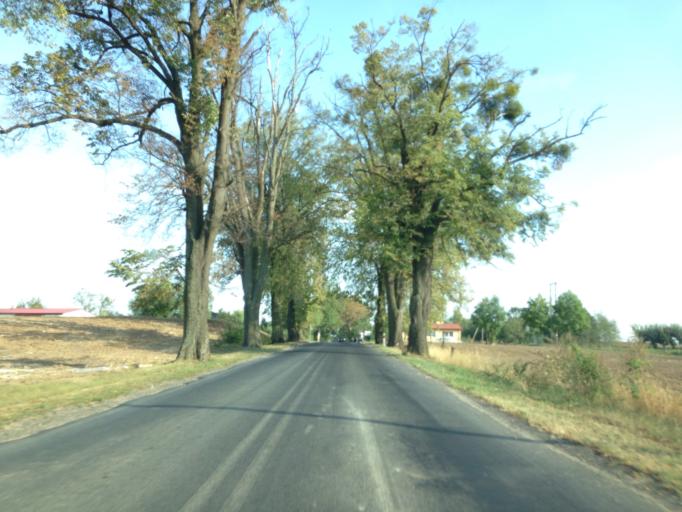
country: PL
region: Kujawsko-Pomorskie
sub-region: Powiat grudziadzki
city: Lasin
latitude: 53.5088
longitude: 19.1757
